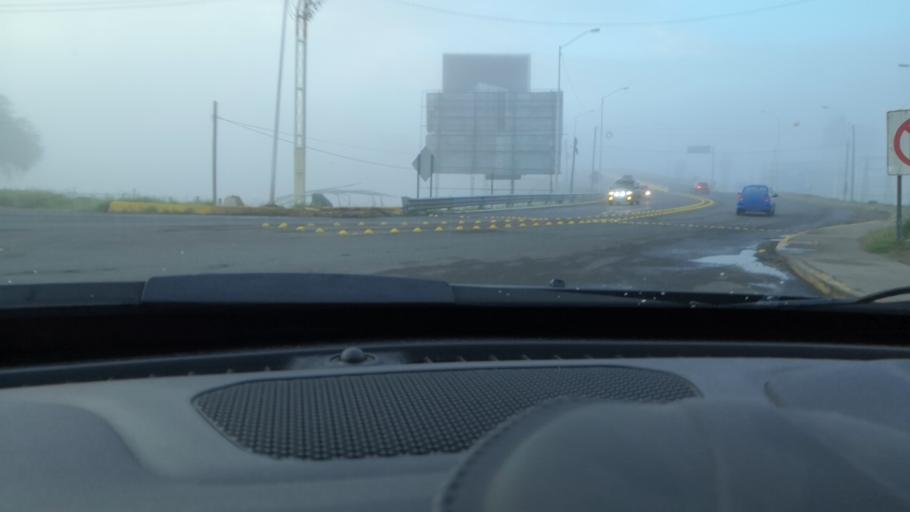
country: MX
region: Guanajuato
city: Colonia Nuevo Mexico
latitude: 20.9838
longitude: -101.4800
